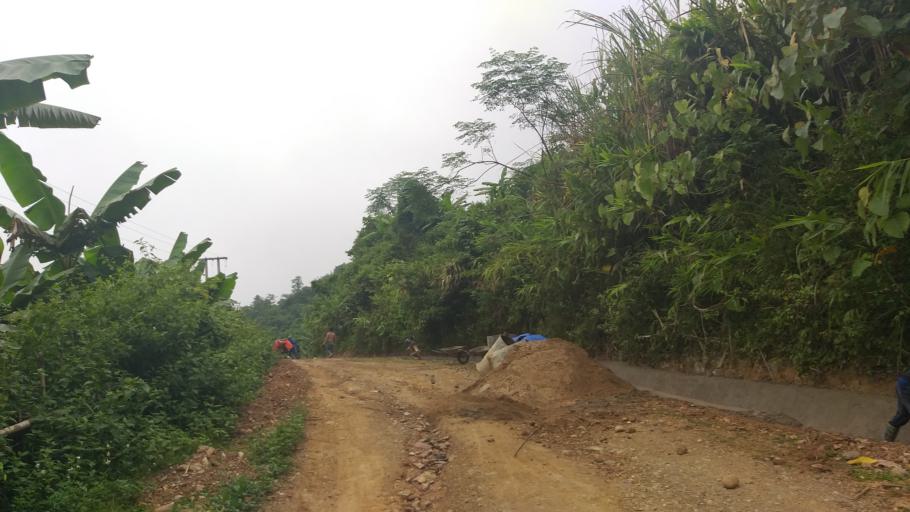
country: LA
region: Phongsali
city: Khoa
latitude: 21.2410
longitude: 102.6709
